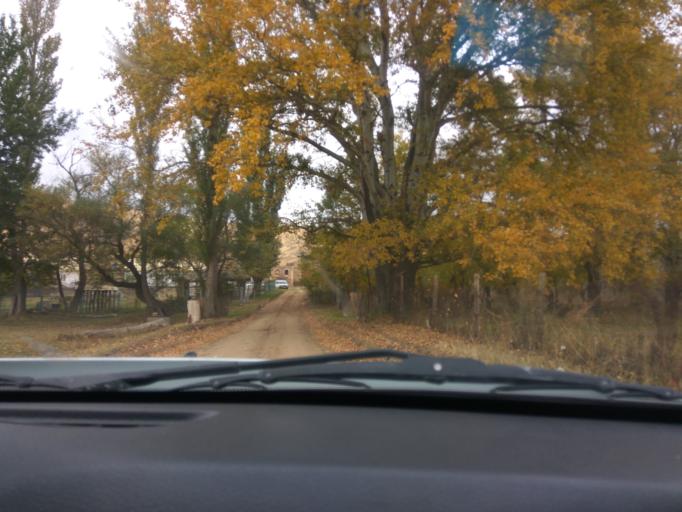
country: RU
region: Dagestan
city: Korkmaskala
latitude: 43.0020
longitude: 47.2388
